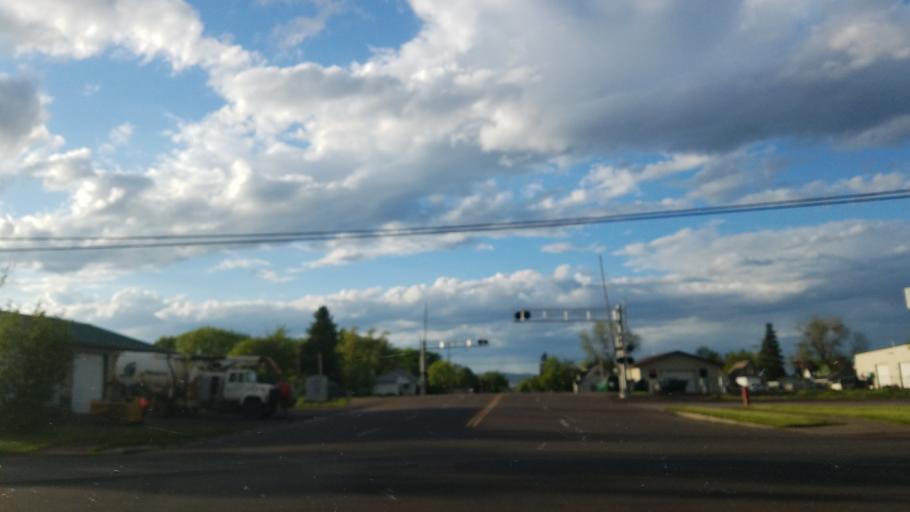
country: US
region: Wisconsin
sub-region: Douglas County
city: Superior
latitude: 46.7276
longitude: -92.0934
